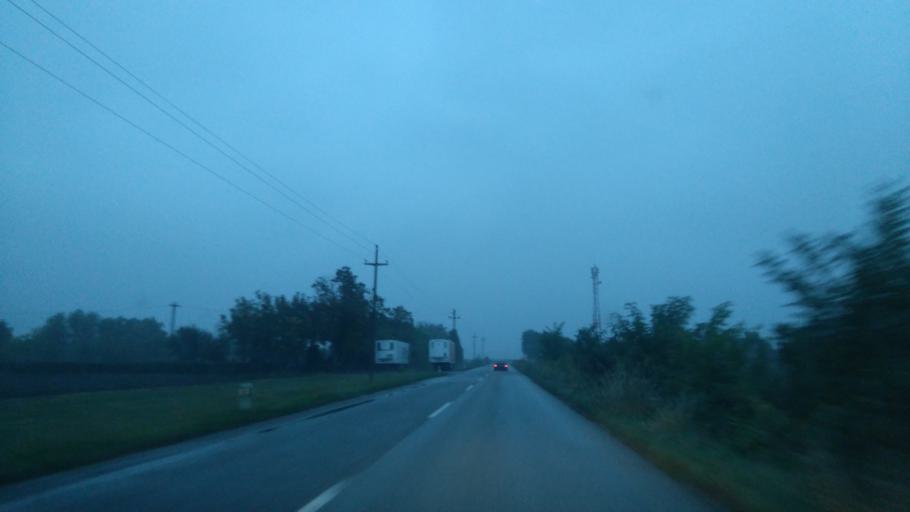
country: RS
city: Backo Petrovo Selo
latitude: 45.7219
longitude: 20.0947
